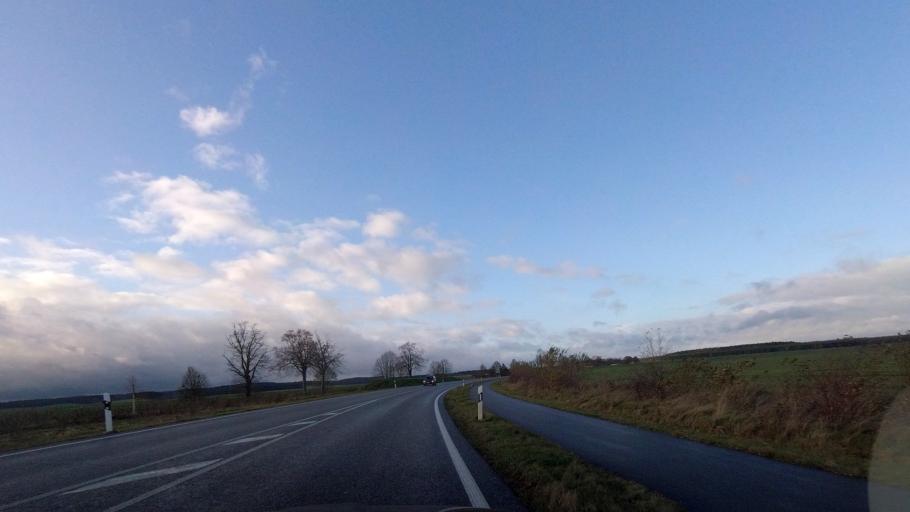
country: DE
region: Brandenburg
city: Niemegk
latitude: 52.1077
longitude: 12.6527
